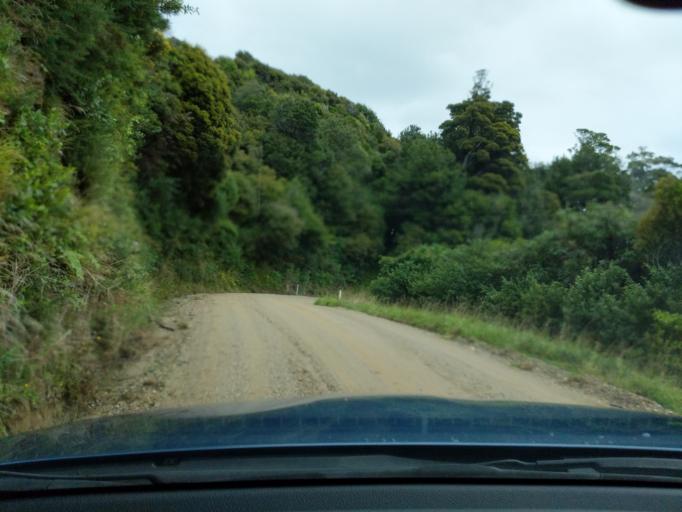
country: NZ
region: Tasman
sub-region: Tasman District
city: Takaka
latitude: -40.6256
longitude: 172.5186
